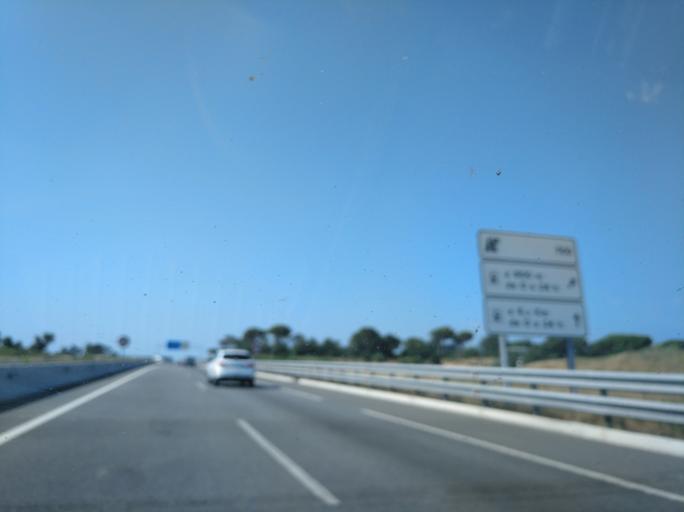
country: ES
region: Catalonia
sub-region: Provincia de Girona
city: Vilobi d'Onyar
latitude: 41.8573
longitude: 2.7746
